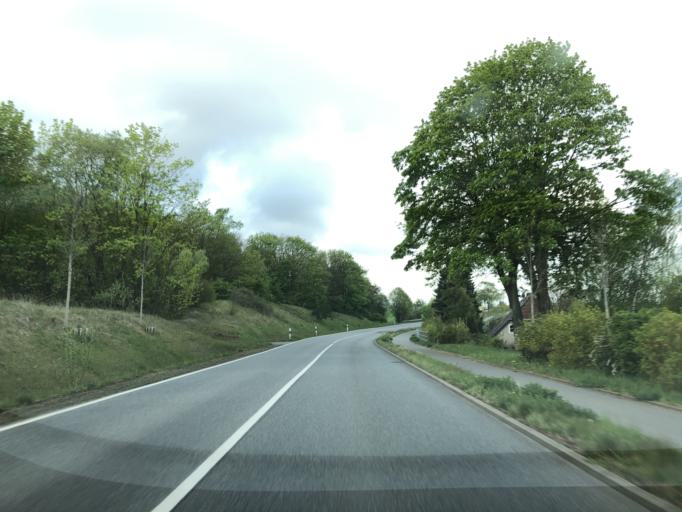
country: DE
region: Mecklenburg-Vorpommern
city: Guestrow
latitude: 53.7653
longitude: 12.1472
